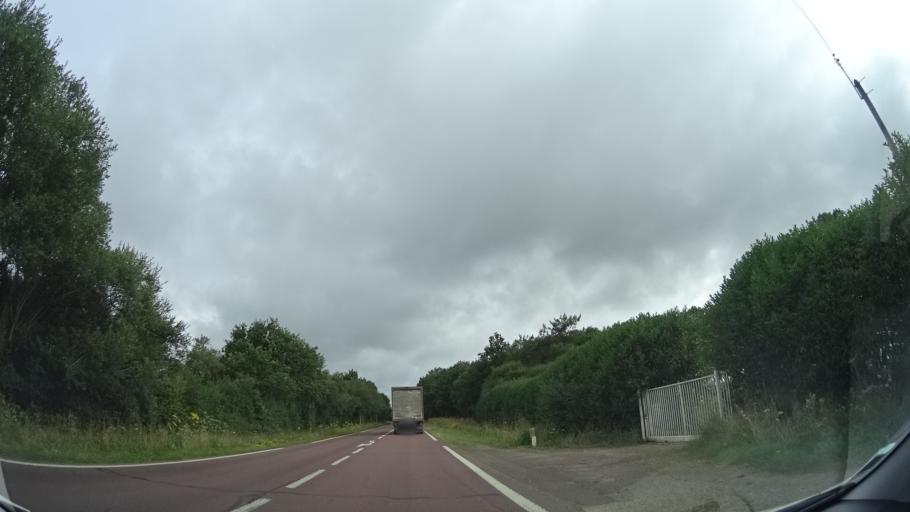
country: FR
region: Lower Normandy
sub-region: Departement de la Manche
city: Pirou
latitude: 49.1407
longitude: -1.5071
